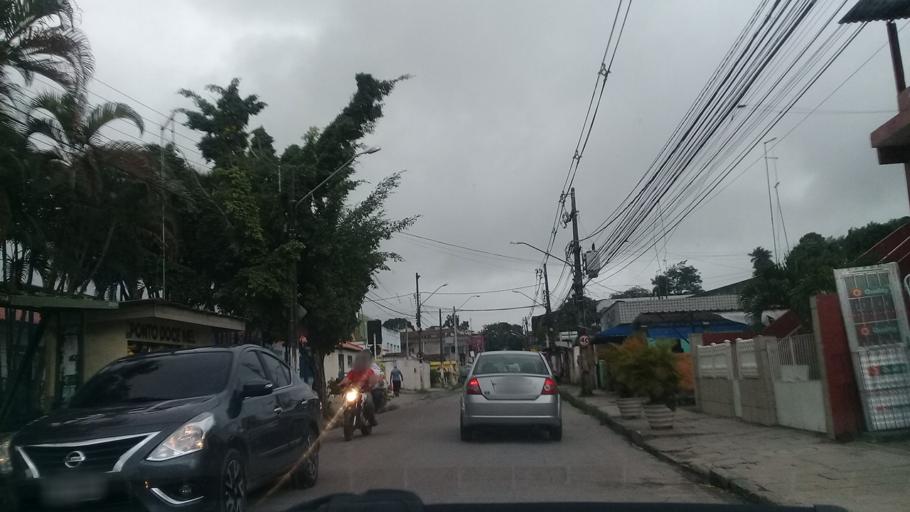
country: BR
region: Pernambuco
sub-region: Moreno
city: Moreno
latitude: -8.1171
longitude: -35.0925
